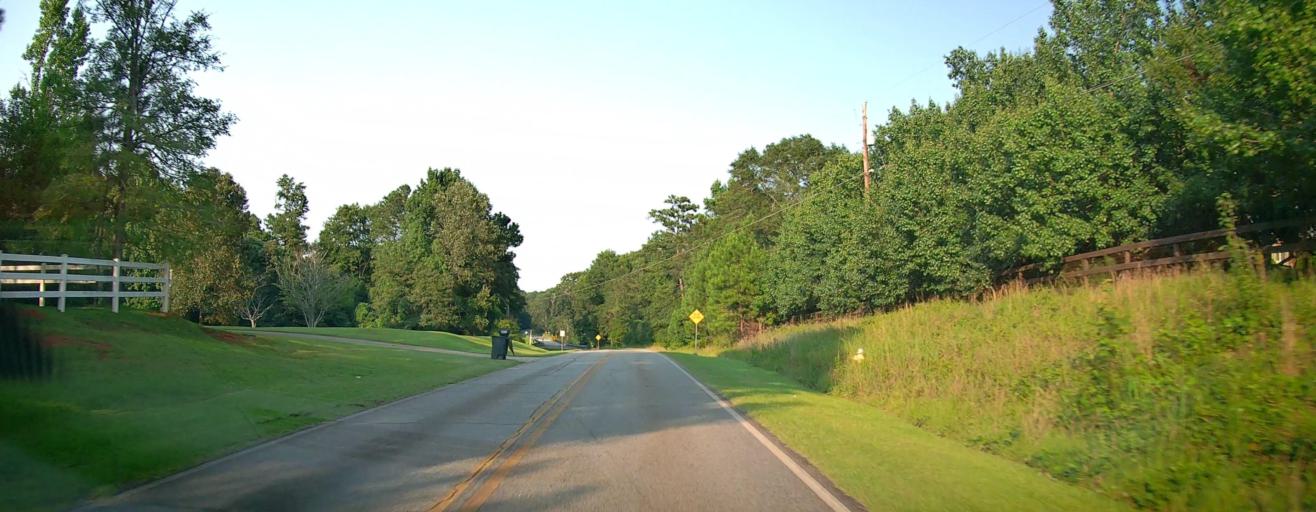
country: US
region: Georgia
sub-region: Bibb County
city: West Point
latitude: 32.8986
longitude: -83.7889
